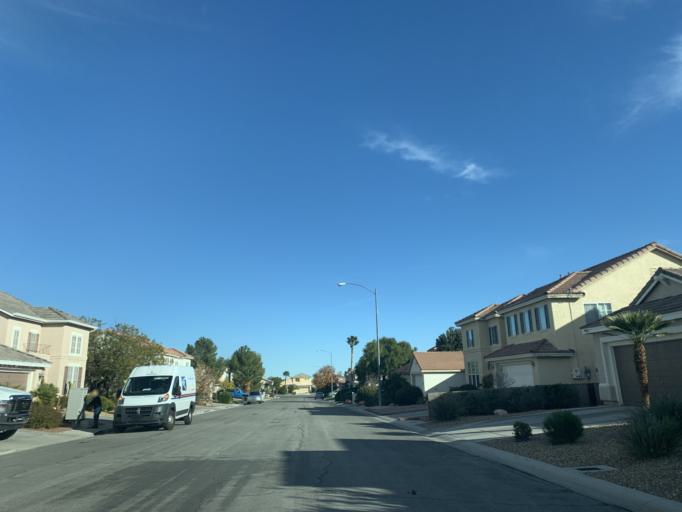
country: US
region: Nevada
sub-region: Clark County
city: Summerlin South
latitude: 36.1272
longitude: -115.3015
